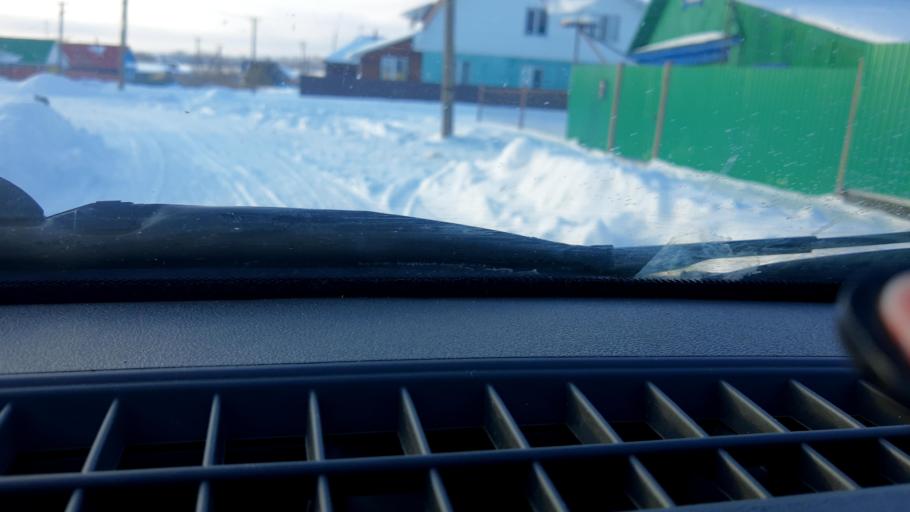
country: RU
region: Bashkortostan
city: Birsk
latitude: 55.1628
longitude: 55.6633
